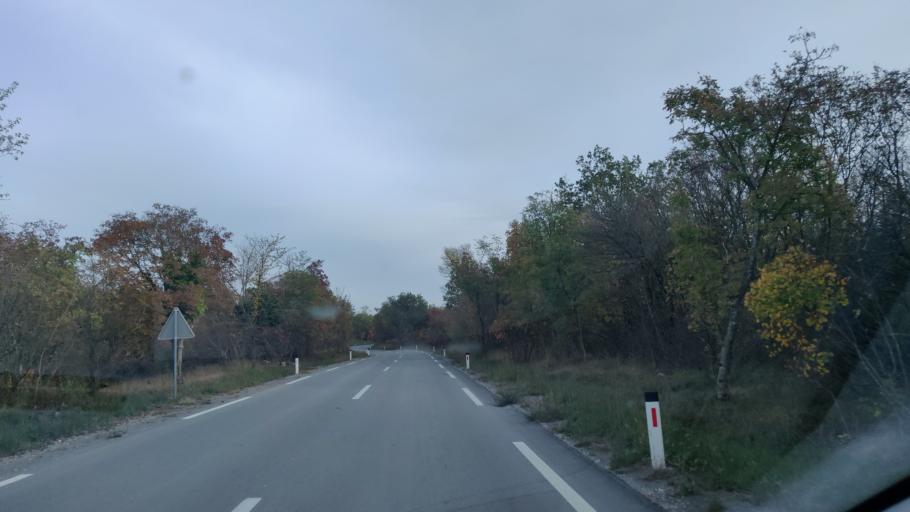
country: SI
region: Miren-Kostanjevica
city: Bilje
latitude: 45.8476
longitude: 13.6217
